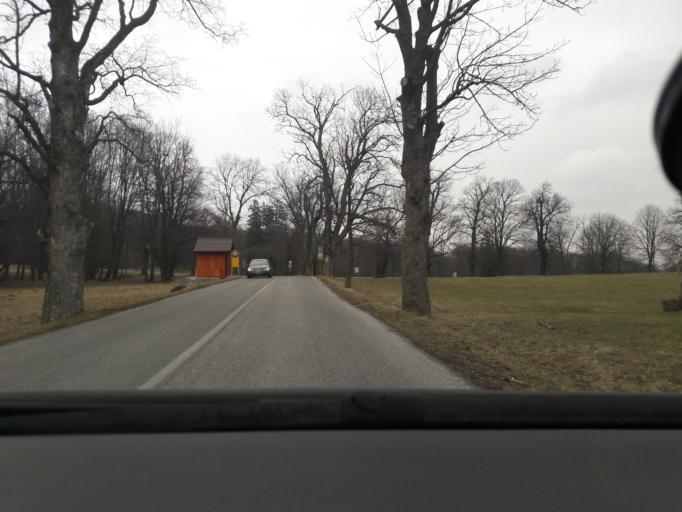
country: SK
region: Bratislavsky
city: Modra
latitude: 48.3955
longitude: 17.3340
